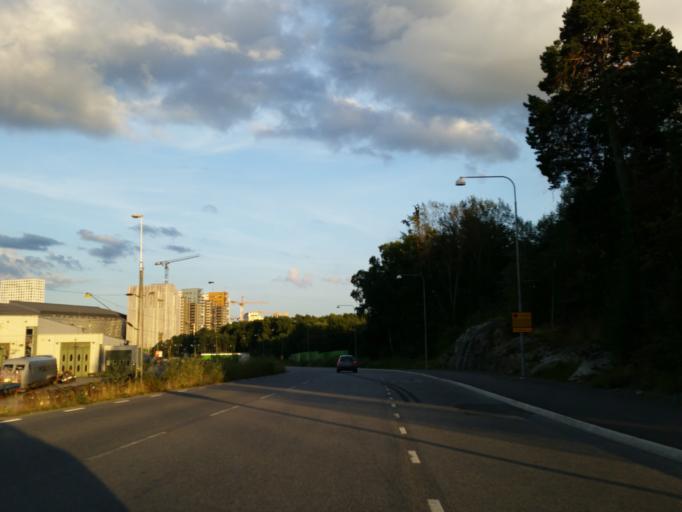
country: SE
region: Stockholm
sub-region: Solna Kommun
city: Rasunda
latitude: 59.3755
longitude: 17.9882
